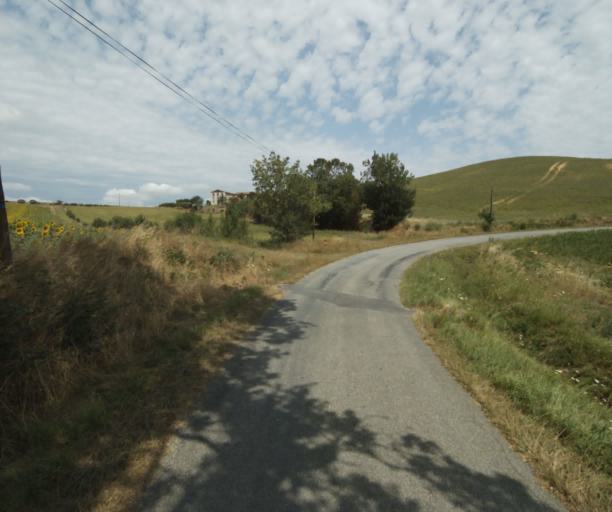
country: FR
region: Midi-Pyrenees
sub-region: Departement de la Haute-Garonne
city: Saint-Felix-Lauragais
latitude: 43.4429
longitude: 1.8868
